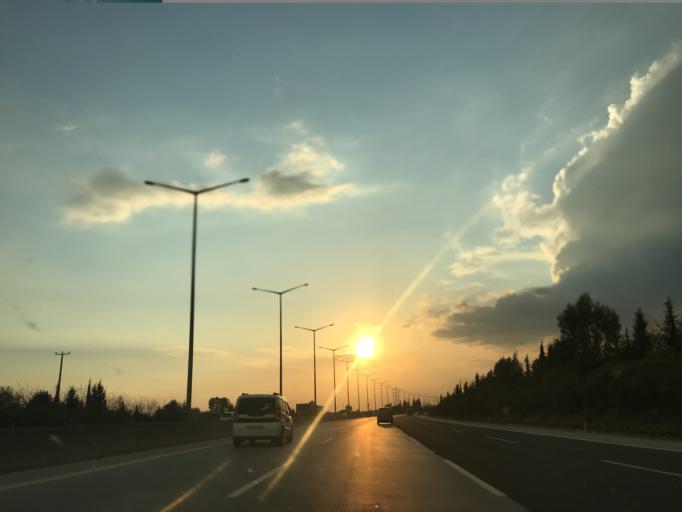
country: TR
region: Adana
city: Seyhan
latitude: 37.0303
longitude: 35.2321
